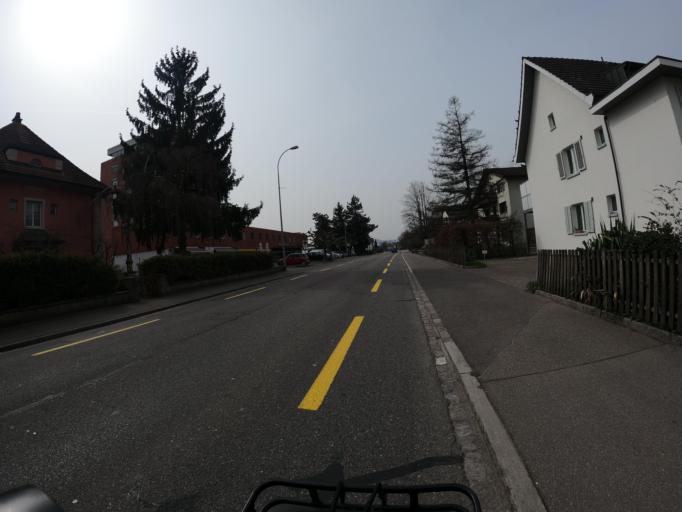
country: CH
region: Aargau
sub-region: Bezirk Aarau
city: Buchs
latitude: 47.4006
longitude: 8.0756
